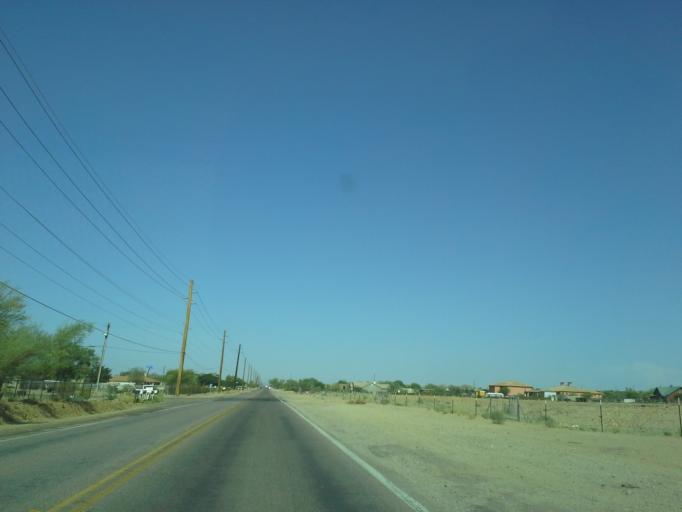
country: US
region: Arizona
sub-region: Maricopa County
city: Queen Creek
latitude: 33.2049
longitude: -111.6484
